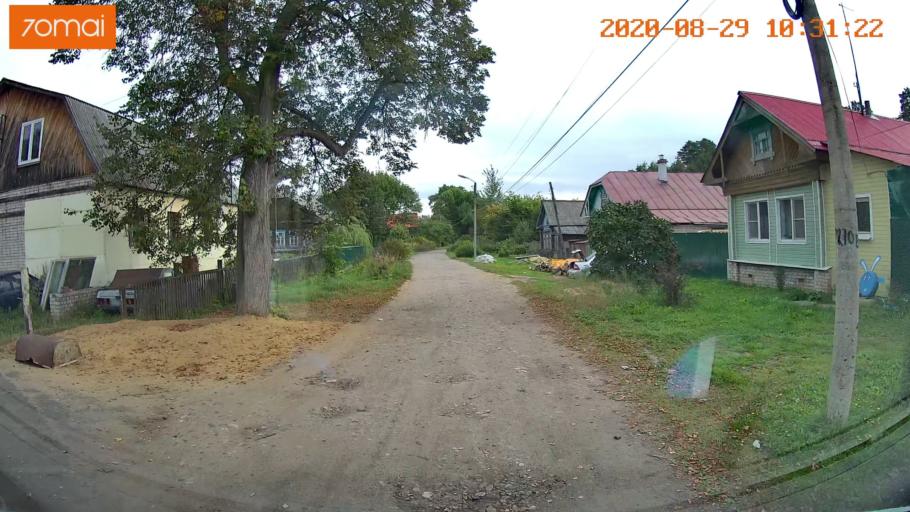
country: RU
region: Ivanovo
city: Yur'yevets
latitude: 57.3155
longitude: 43.1027
